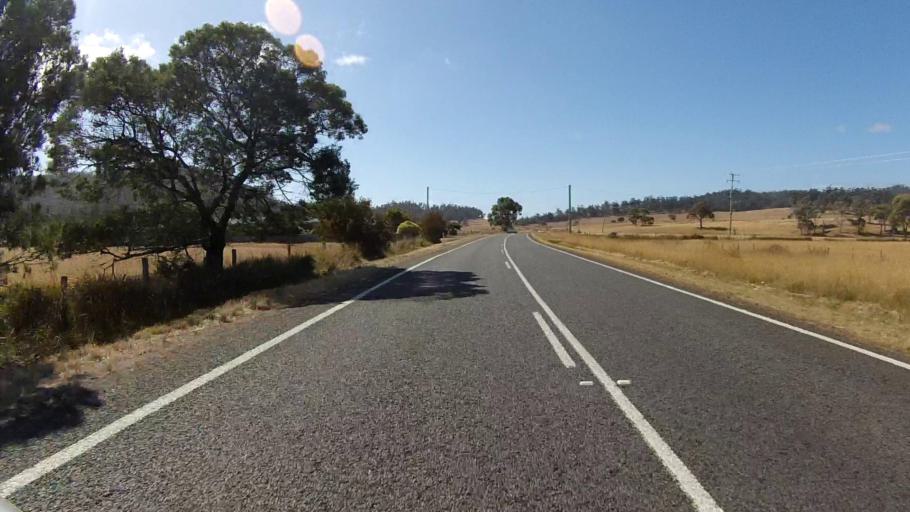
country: AU
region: Tasmania
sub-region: Sorell
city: Sorell
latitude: -42.4411
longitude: 147.9280
